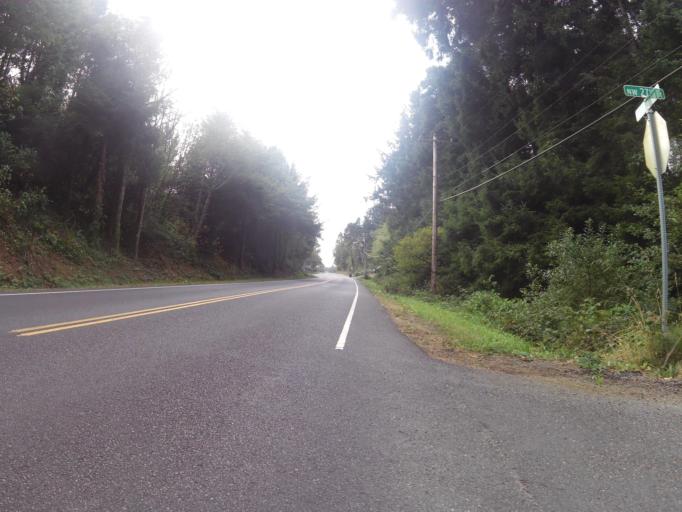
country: US
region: Oregon
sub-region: Lincoln County
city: Newport
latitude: 44.6555
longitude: -124.0562
